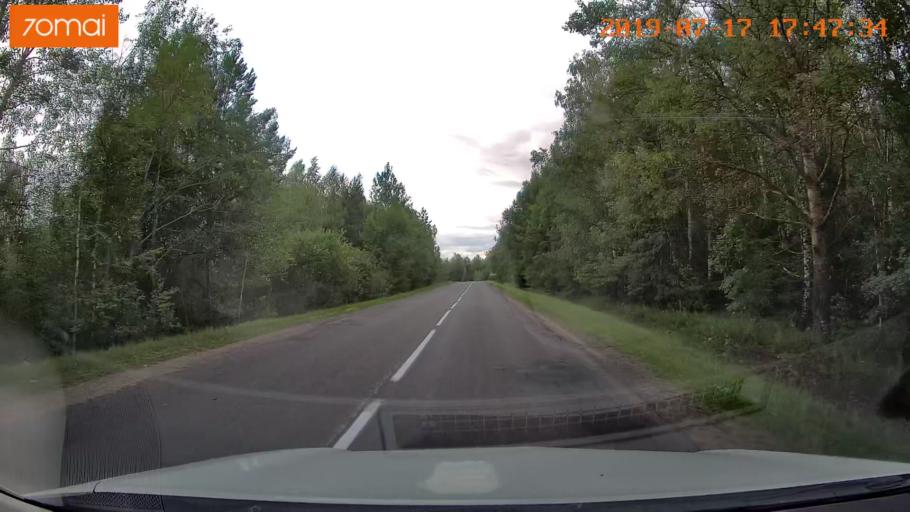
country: BY
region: Mogilev
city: Hlusha
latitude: 53.1125
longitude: 28.8291
